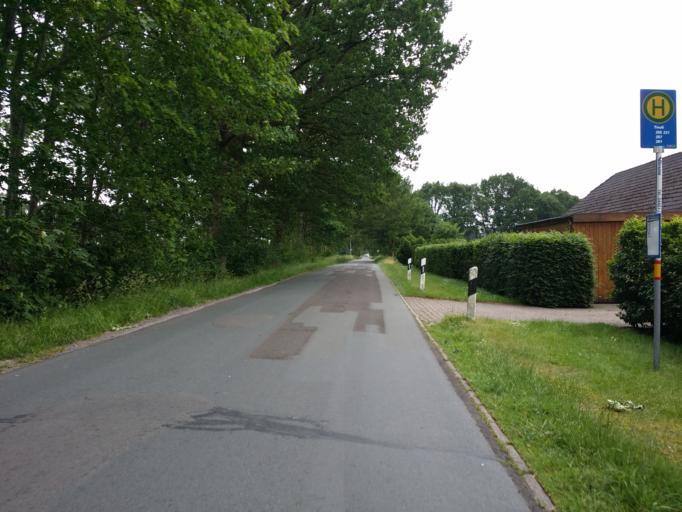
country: DE
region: Lower Saxony
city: Bockhorn
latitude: 53.3570
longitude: 8.0100
